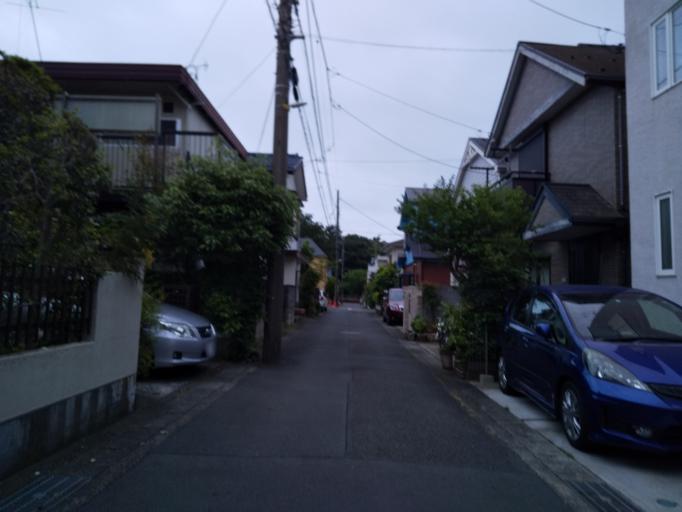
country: JP
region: Tokyo
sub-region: Machida-shi
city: Machida
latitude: 35.5621
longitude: 139.3911
